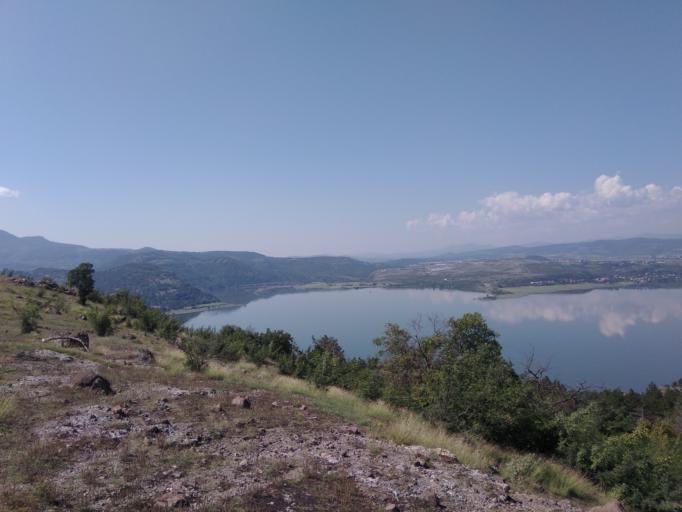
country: BG
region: Kurdzhali
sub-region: Obshtina Kurdzhali
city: Kurdzhali
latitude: 41.6298
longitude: 25.4518
